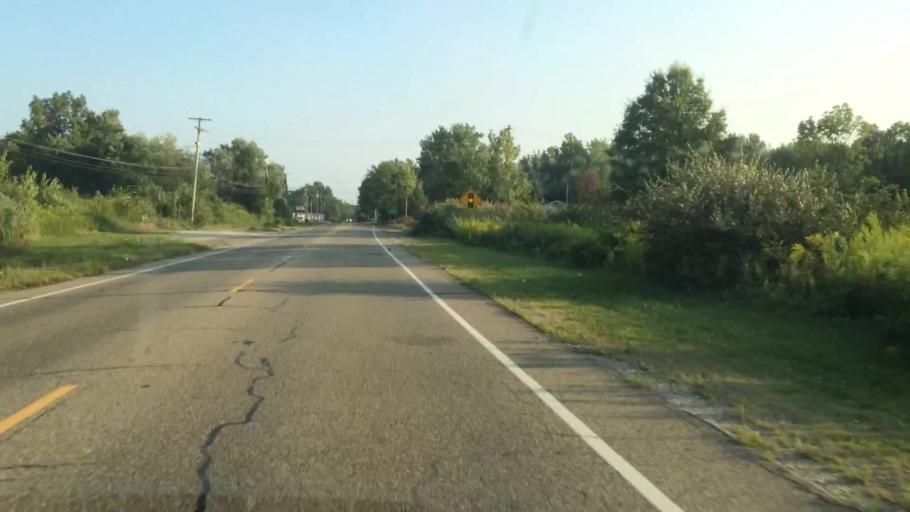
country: US
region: Ohio
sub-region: Summit County
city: Boston Heights
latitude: 41.2226
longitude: -81.4908
